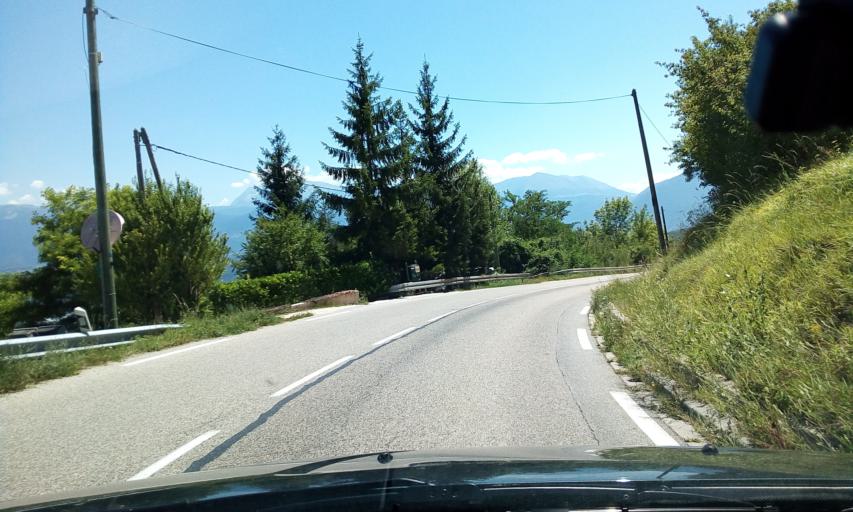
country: FR
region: Rhone-Alpes
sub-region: Departement de l'Isere
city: Seyssins
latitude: 45.1661
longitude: 5.6681
